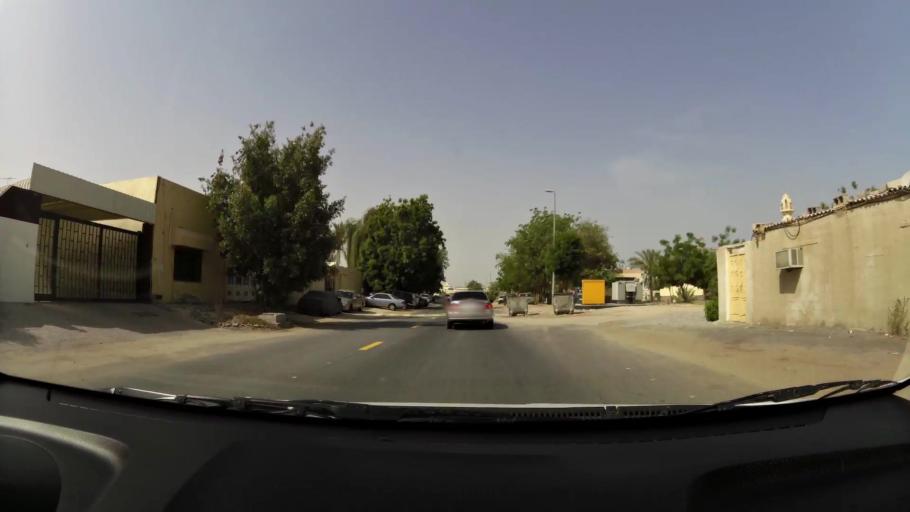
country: AE
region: Ash Shariqah
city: Sharjah
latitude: 25.3501
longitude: 55.4124
